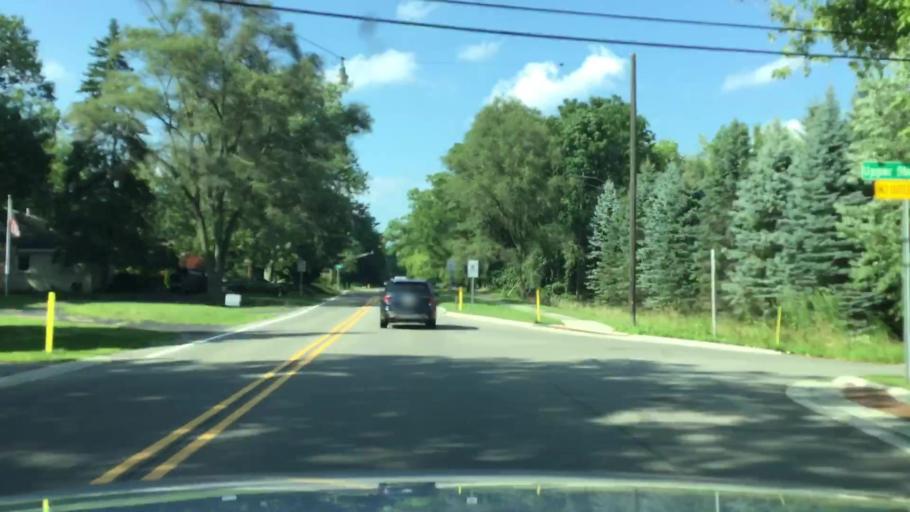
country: US
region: Michigan
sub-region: Oakland County
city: West Bloomfield Township
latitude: 42.5801
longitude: -83.4117
